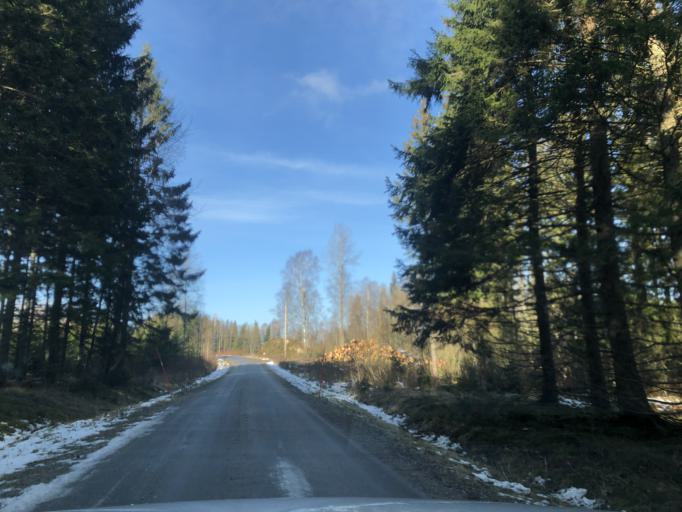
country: SE
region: Vaestra Goetaland
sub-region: Ulricehamns Kommun
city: Ulricehamn
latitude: 57.7948
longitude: 13.4569
